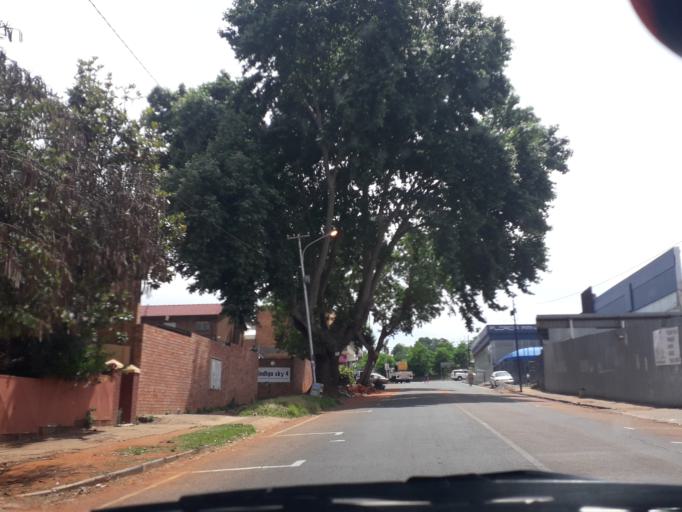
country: ZA
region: Gauteng
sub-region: City of Johannesburg Metropolitan Municipality
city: Roodepoort
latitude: -26.1763
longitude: 27.9111
